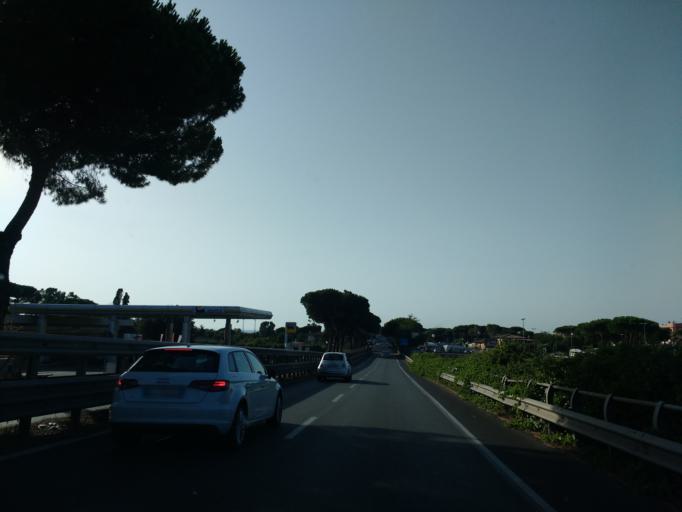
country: IT
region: Latium
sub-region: Citta metropolitana di Roma Capitale
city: Marino
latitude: 41.7729
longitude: 12.6108
